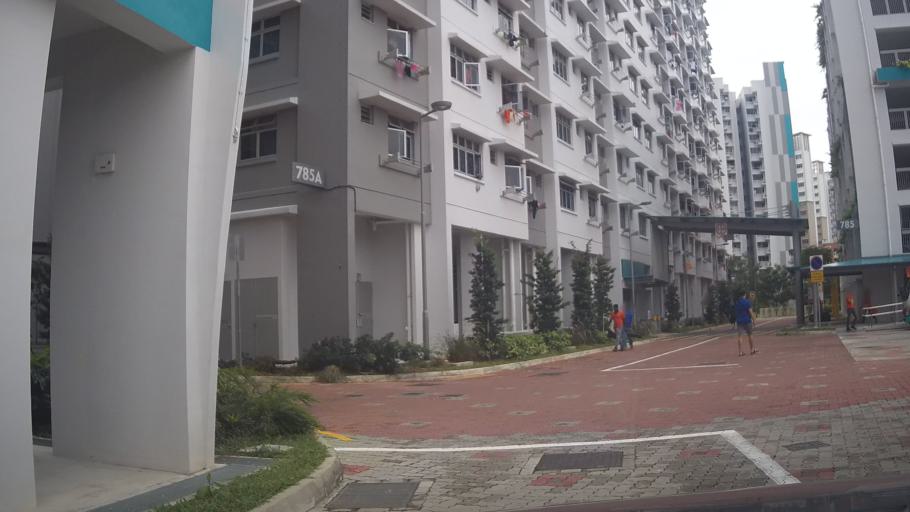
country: MY
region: Johor
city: Johor Bahru
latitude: 1.4467
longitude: 103.8054
